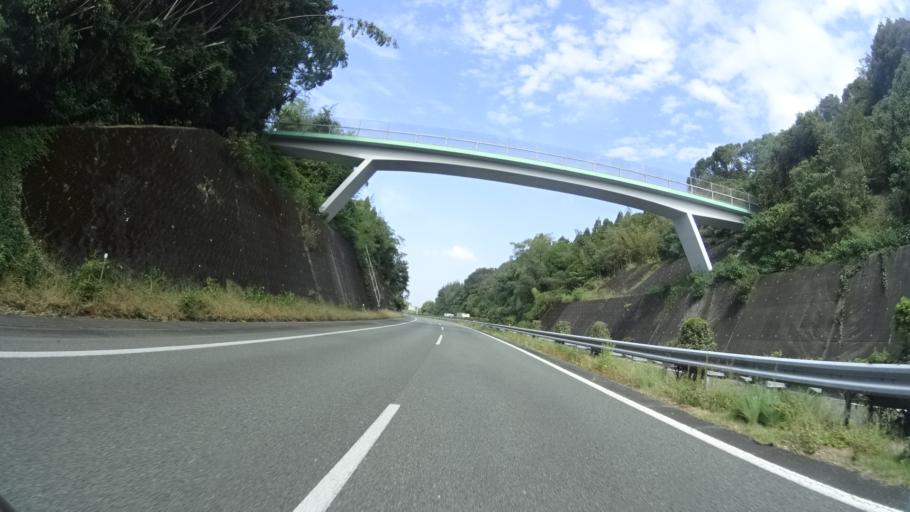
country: JP
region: Kumamoto
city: Matsubase
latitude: 32.6259
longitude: 130.7125
